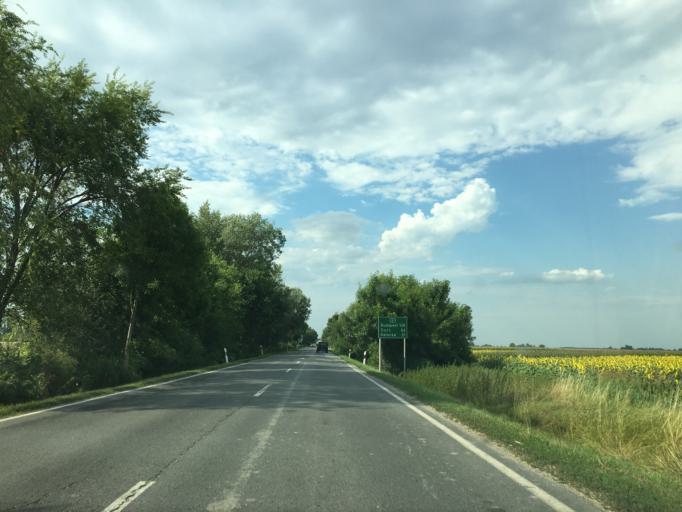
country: HU
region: Bacs-Kiskun
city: Dusnok
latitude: 46.3558
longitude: 18.9648
